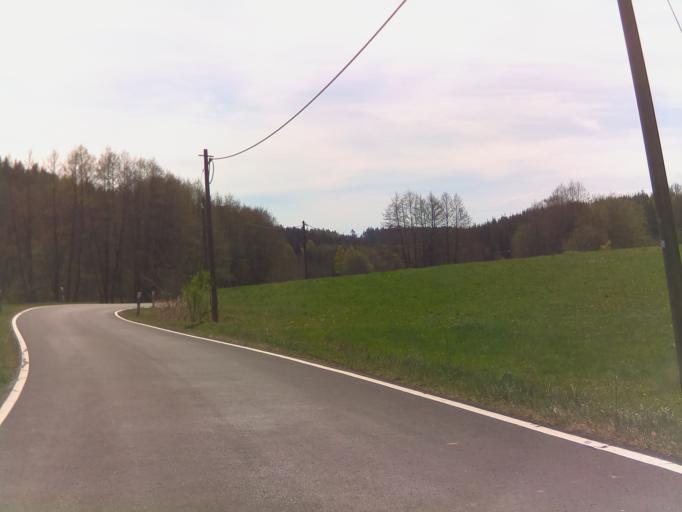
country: DE
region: Thuringia
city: Hellingen
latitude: 50.2514
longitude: 10.6614
